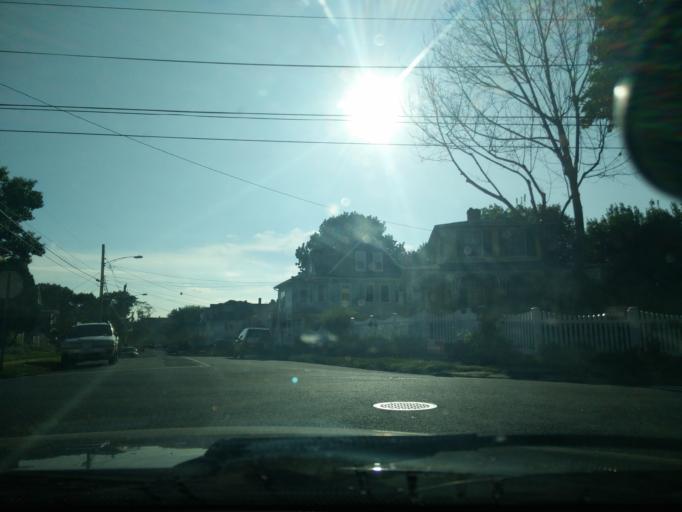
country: US
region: Connecticut
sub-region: Fairfield County
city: Bridgeport
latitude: 41.1632
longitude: -73.2236
